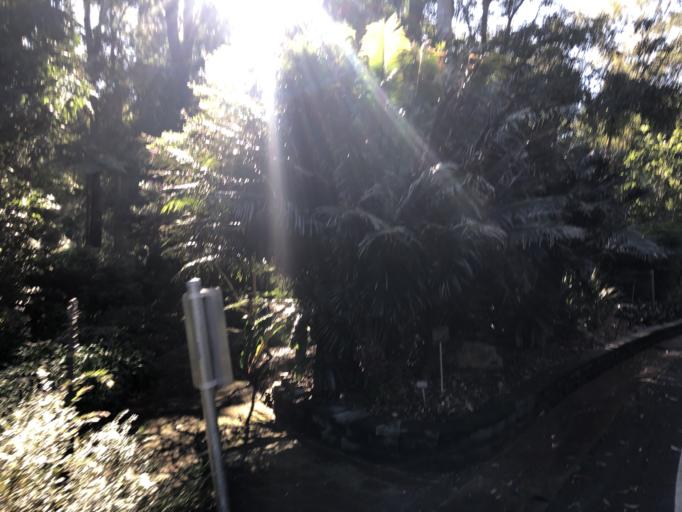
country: AU
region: New South Wales
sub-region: Coffs Harbour
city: Coffs Harbour
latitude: -30.2983
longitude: 153.1243
